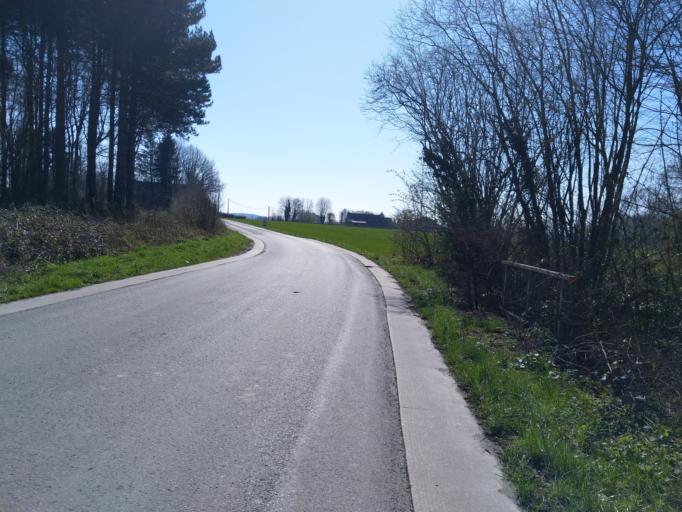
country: BE
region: Wallonia
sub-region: Province du Hainaut
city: Soignies
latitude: 50.5288
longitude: 4.0046
